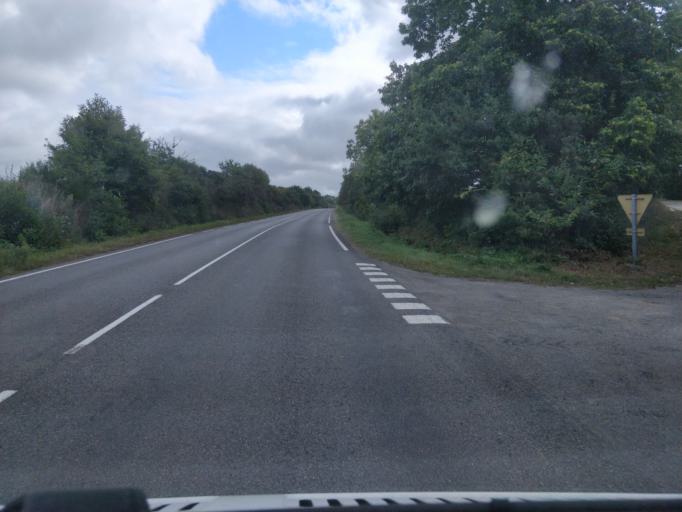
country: FR
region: Brittany
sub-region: Departement du Finistere
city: Plogastel-Saint-Germain
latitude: 47.9954
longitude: -4.2426
